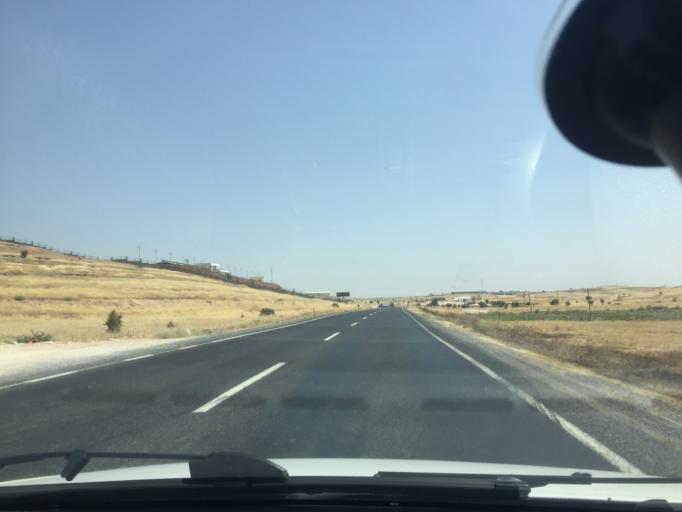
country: TR
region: Mardin
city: Kindirip
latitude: 37.4581
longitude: 41.2410
